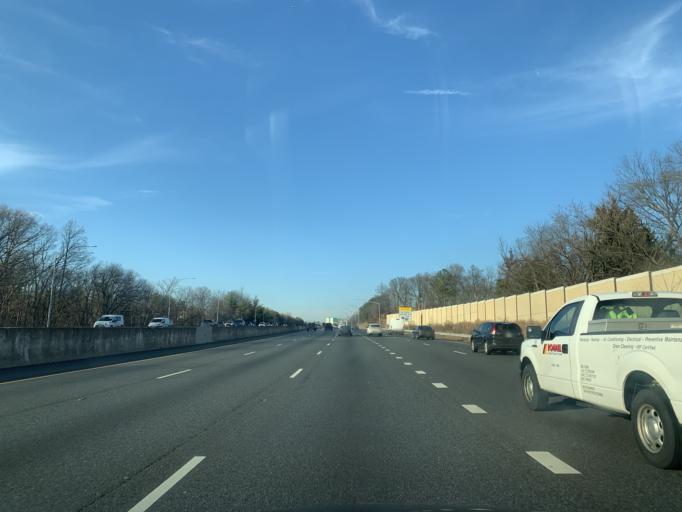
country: US
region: Maryland
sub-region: Baltimore County
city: Pikesville
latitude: 39.3633
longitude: -76.7468
